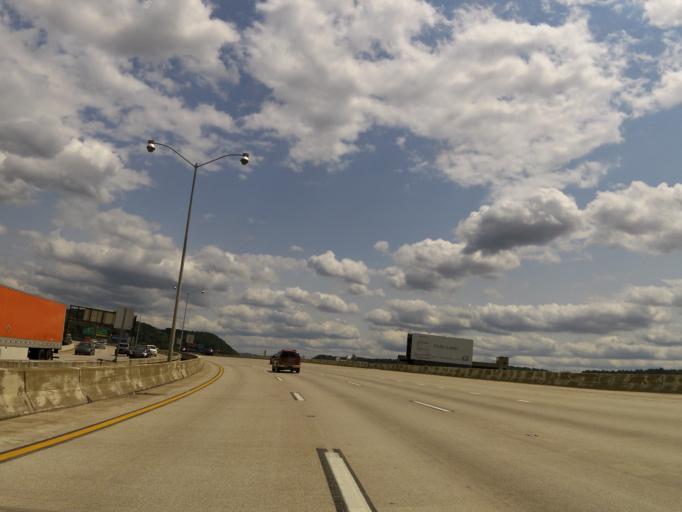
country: US
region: West Virginia
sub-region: Kanawha County
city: Charleston
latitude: 38.3544
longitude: -81.6313
